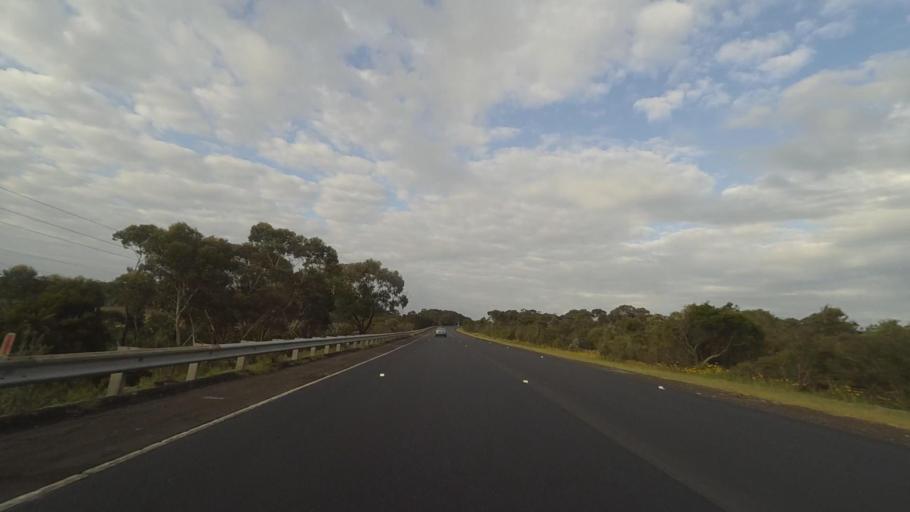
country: AU
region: New South Wales
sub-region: Wollongong
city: Bulli
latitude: -34.2514
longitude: 150.9342
